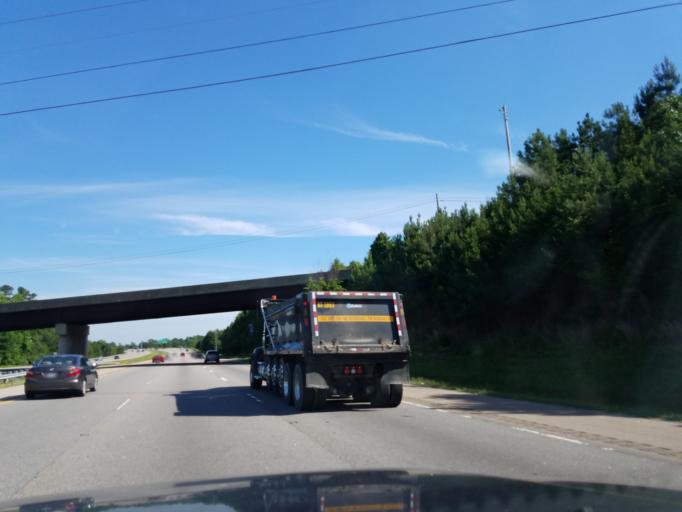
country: US
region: North Carolina
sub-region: Wake County
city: West Raleigh
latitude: 35.8848
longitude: -78.5913
